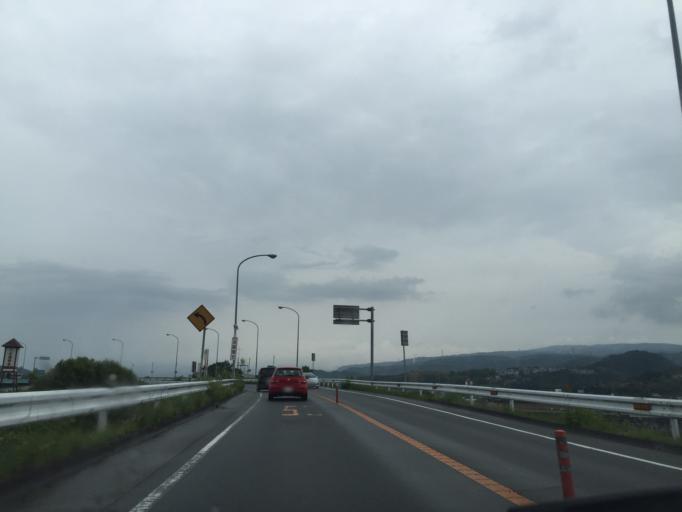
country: JP
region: Shizuoka
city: Mishima
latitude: 35.0188
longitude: 138.9396
